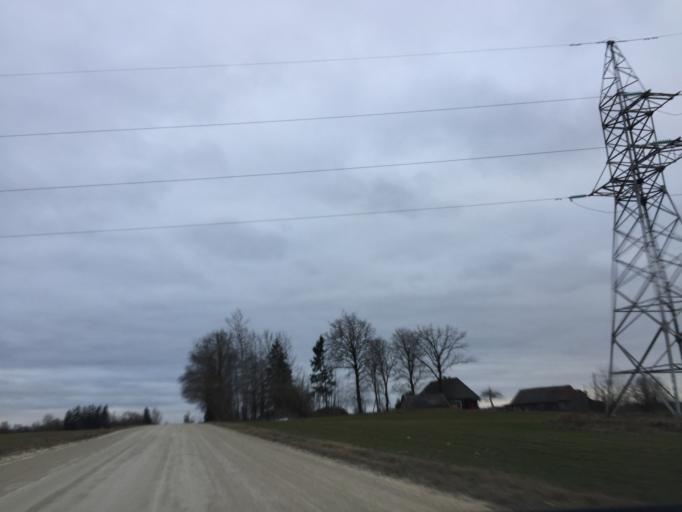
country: LT
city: Zagare
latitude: 56.3377
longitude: 23.2477
